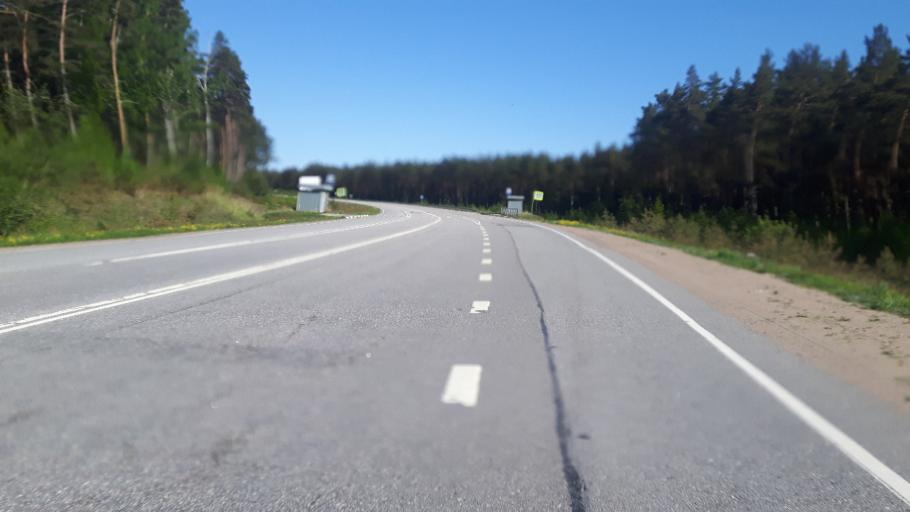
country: RU
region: Leningrad
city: Sosnovyy Bor
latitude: 60.1854
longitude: 29.0276
